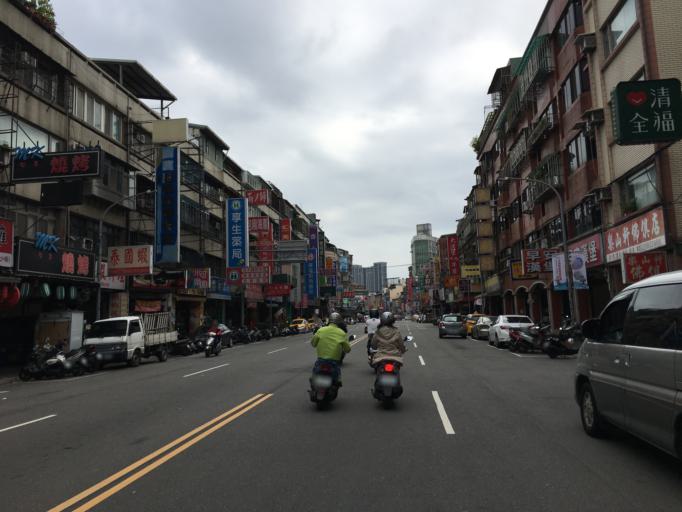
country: TW
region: Taipei
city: Taipei
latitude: 25.0686
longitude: 121.4911
